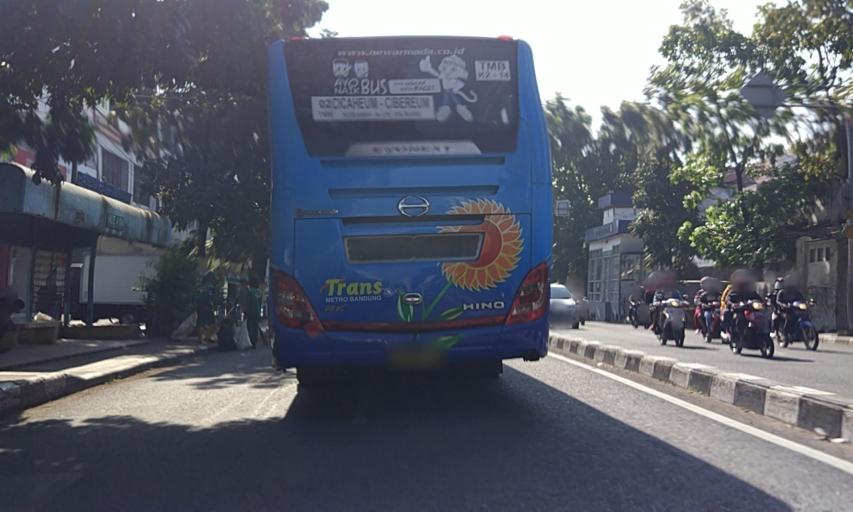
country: ID
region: West Java
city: Bandung
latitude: -6.9181
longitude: 107.6255
